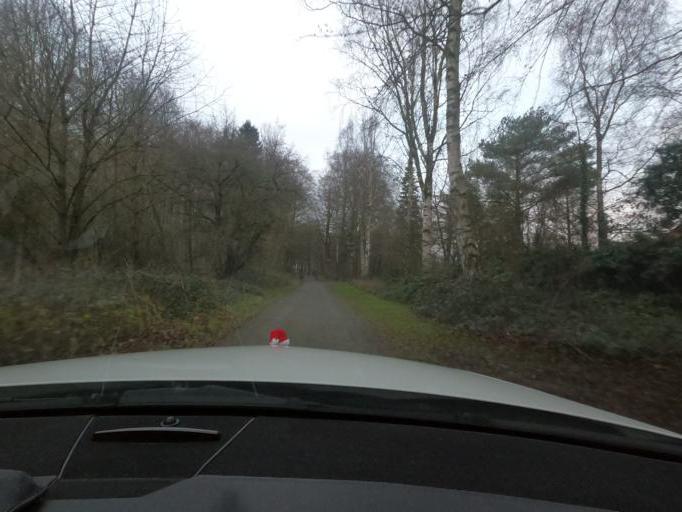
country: DK
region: South Denmark
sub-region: Sonderborg Kommune
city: Sonderborg
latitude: 54.8975
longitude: 9.8509
